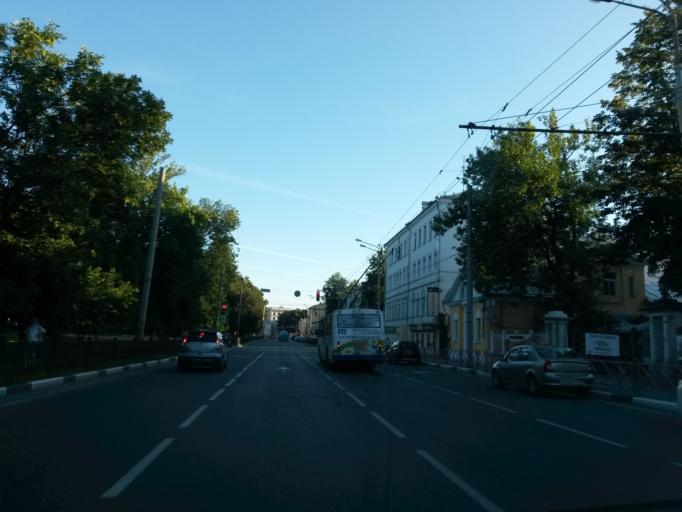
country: RU
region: Jaroslavl
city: Yaroslavl
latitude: 57.6296
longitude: 39.8858
